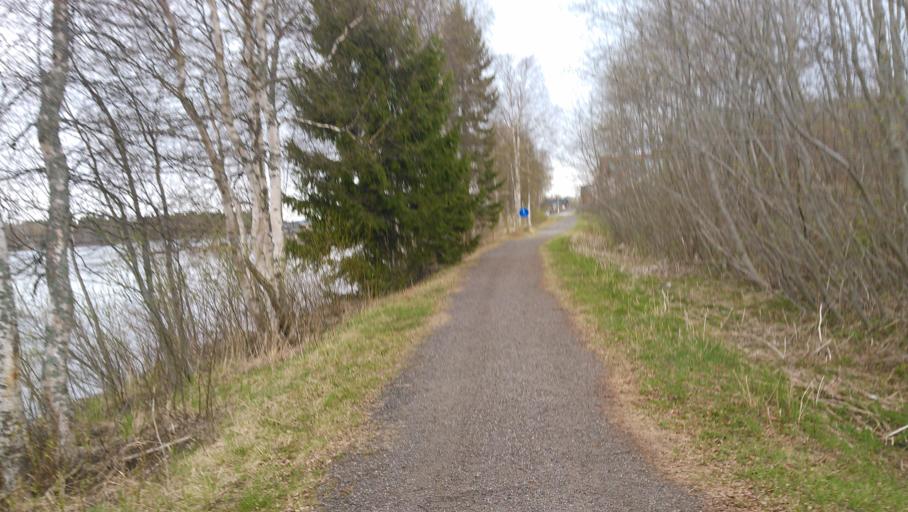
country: SE
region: Vaesterbotten
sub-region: Umea Kommun
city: Umea
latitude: 63.7867
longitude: 20.3109
